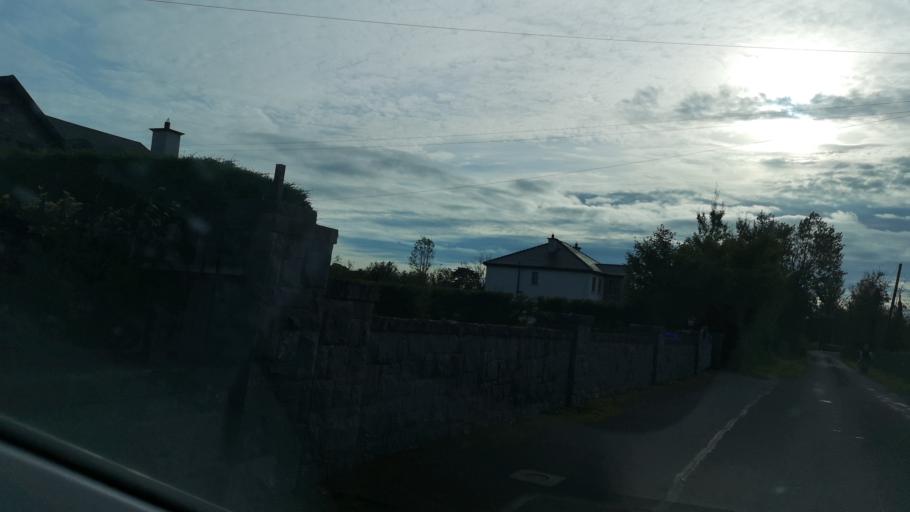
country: IE
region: Connaught
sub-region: County Galway
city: Ballinasloe
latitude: 53.3412
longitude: -8.2632
